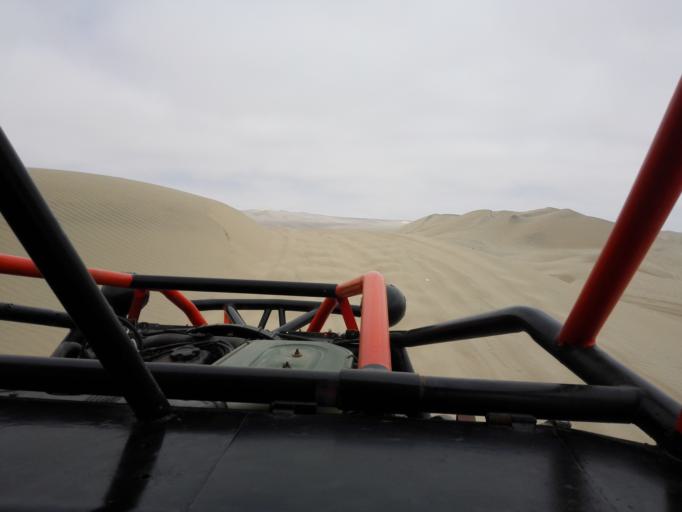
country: PE
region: Ica
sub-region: Provincia de Ica
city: Ica
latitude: -14.0868
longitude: -75.7739
